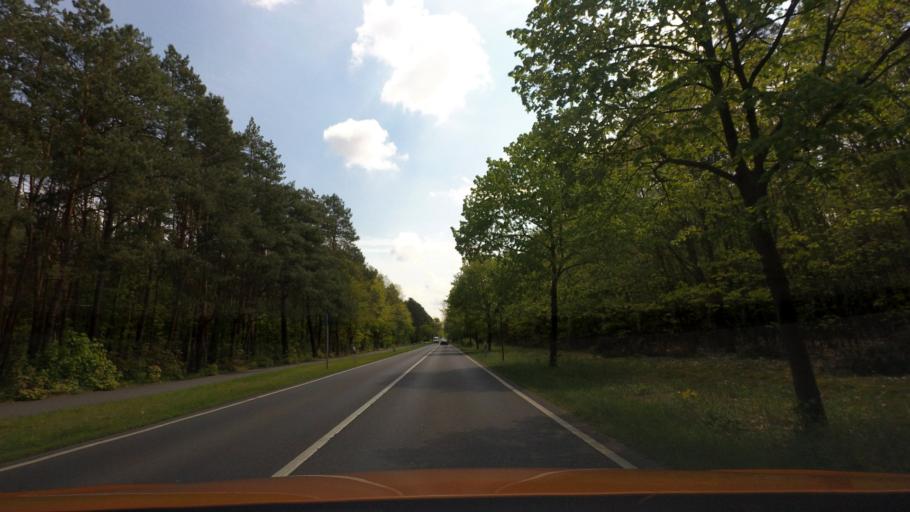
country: DE
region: Brandenburg
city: Zeuthen
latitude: 52.3964
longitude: 13.6100
